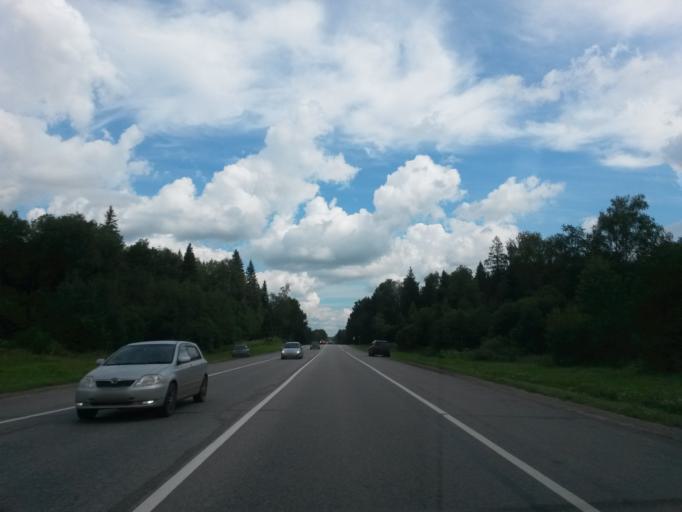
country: RU
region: Jaroslavl
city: Pereslavl'-Zalesskiy
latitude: 56.6358
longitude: 38.6765
